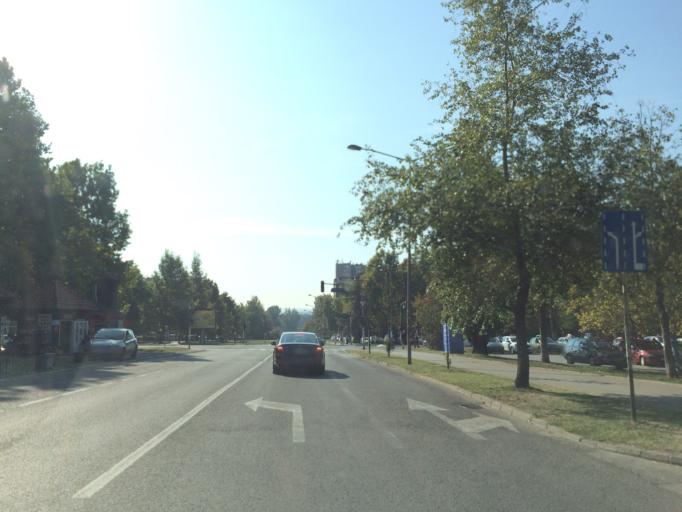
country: RS
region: Autonomna Pokrajina Vojvodina
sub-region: Juznobacki Okrug
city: Novi Sad
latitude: 45.2394
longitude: 19.8321
